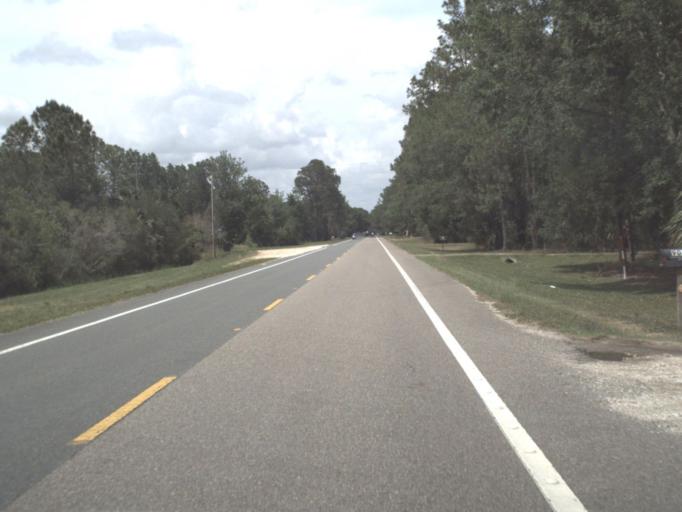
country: US
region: Florida
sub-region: Flagler County
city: Bunnell
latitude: 29.3499
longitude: -81.3112
